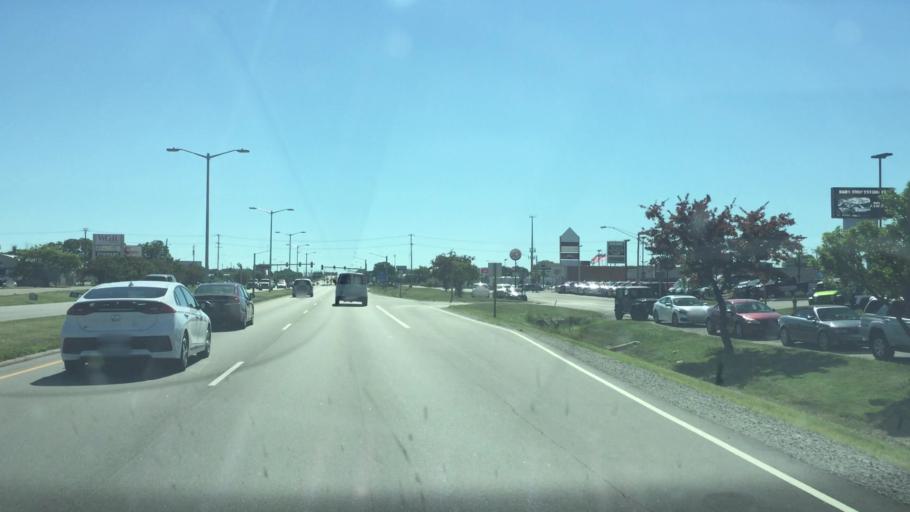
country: US
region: Wisconsin
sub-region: Outagamie County
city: Appleton
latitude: 44.2612
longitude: -88.4491
